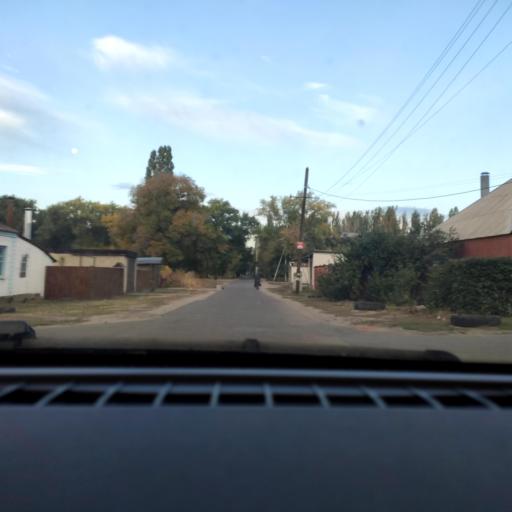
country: RU
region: Voronezj
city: Voronezh
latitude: 51.6685
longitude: 39.2572
